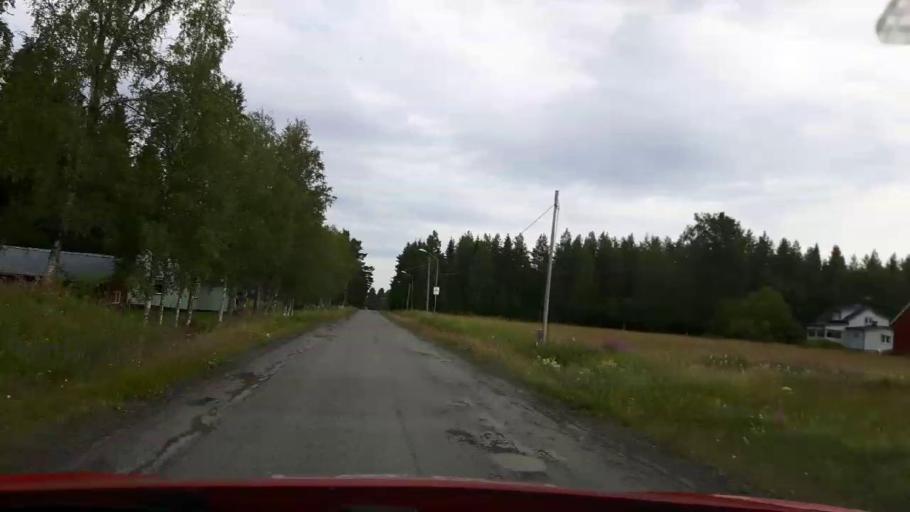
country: SE
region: Jaemtland
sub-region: Stroemsunds Kommun
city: Stroemsund
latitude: 63.5167
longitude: 15.3469
